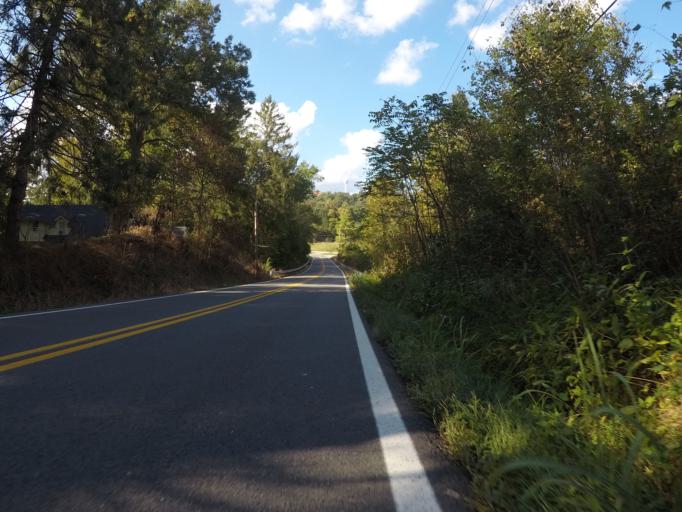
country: US
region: Ohio
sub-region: Lawrence County
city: Burlington
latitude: 38.3700
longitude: -82.5129
